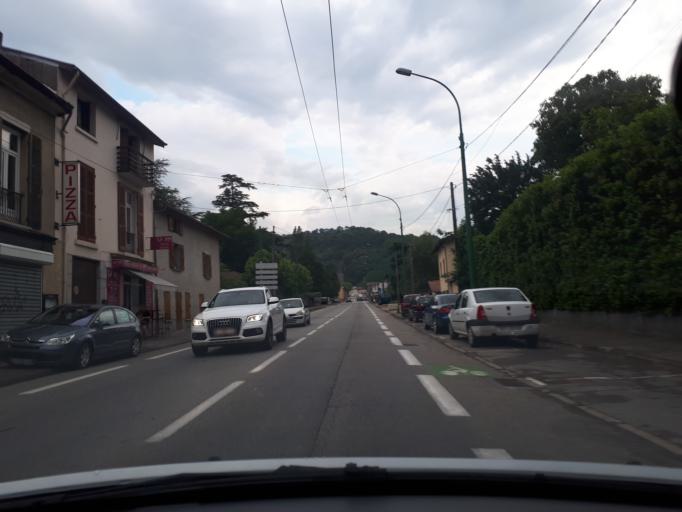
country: FR
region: Rhone-Alpes
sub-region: Departement de l'Isere
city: Eybens
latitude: 45.1520
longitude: 5.7491
